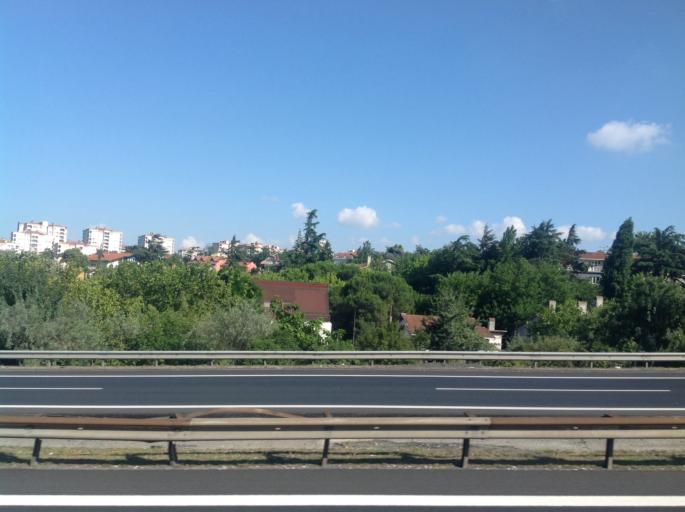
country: TR
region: Istanbul
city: Sisli
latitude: 41.0872
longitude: 29.0157
